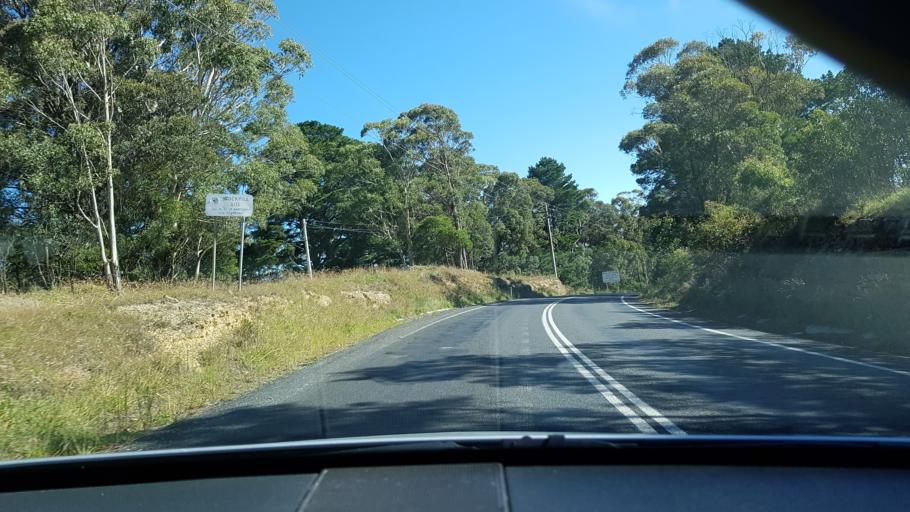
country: AU
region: New South Wales
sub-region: Lithgow
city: Bowenfels
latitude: -33.6392
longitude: 150.0636
